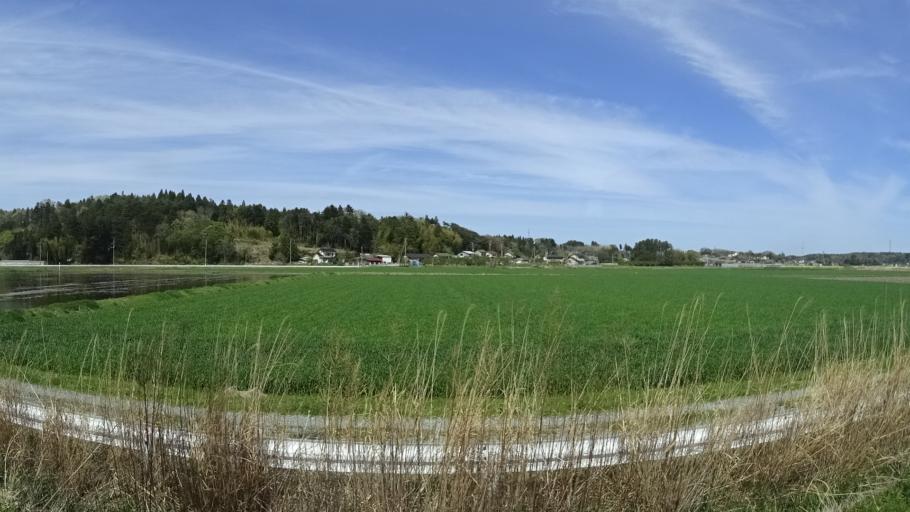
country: JP
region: Fukushima
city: Namie
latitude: 37.6079
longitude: 140.9881
